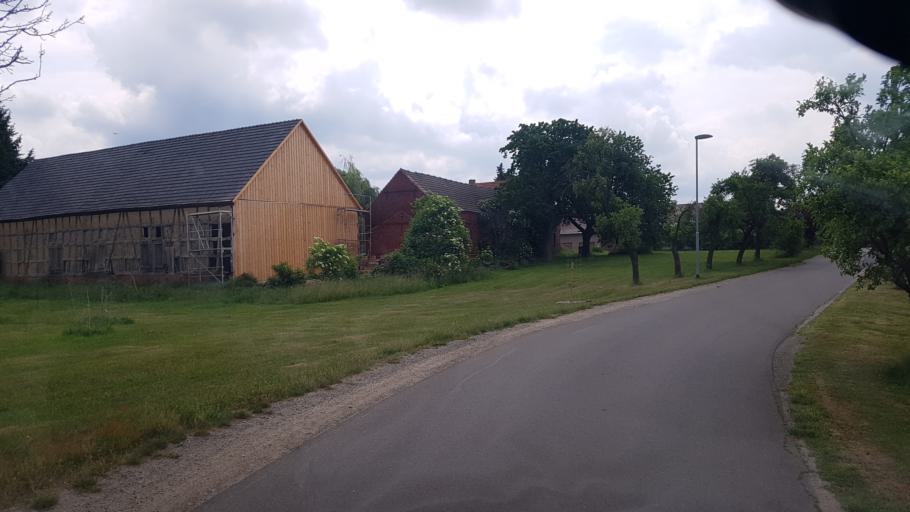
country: DE
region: Brandenburg
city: Lebusa
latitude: 51.8251
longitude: 13.4494
